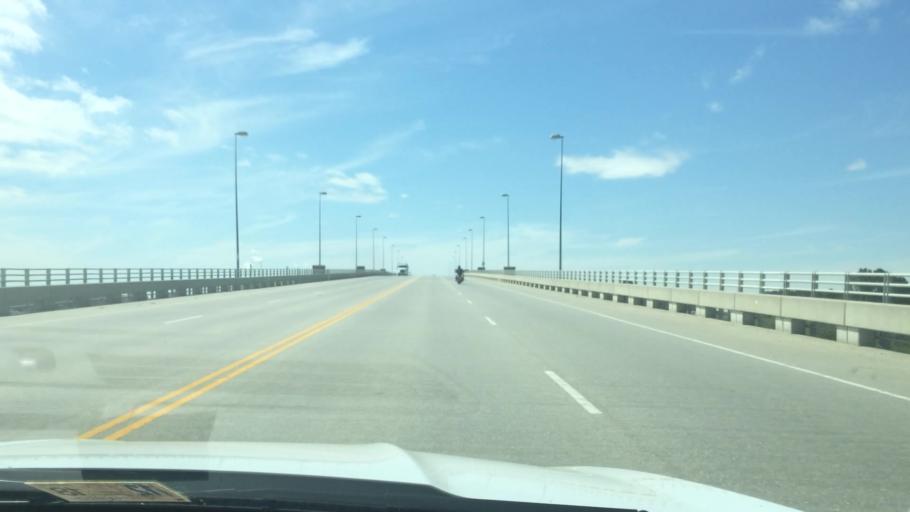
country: US
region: Virginia
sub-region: King William County
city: West Point
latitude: 37.5361
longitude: -76.7841
